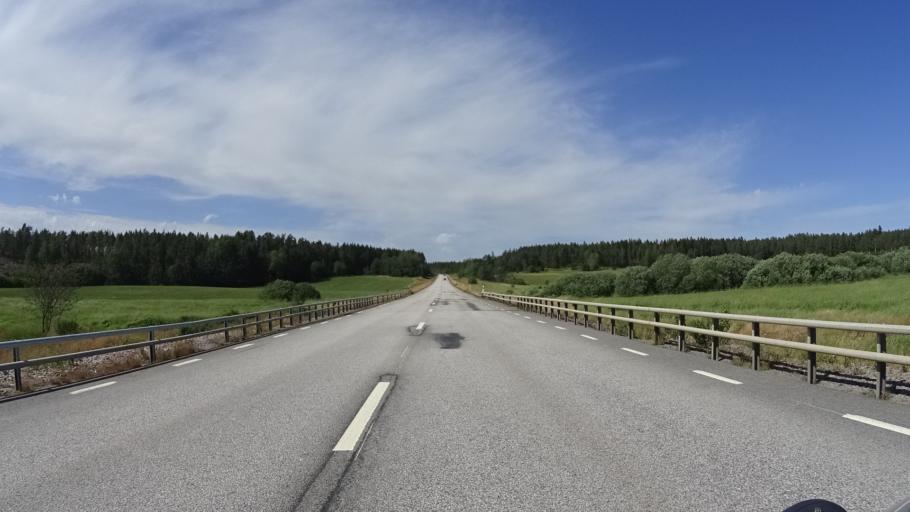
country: SE
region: Kalmar
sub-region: Vasterviks Kommun
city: Gamleby
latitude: 57.9464
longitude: 16.3821
